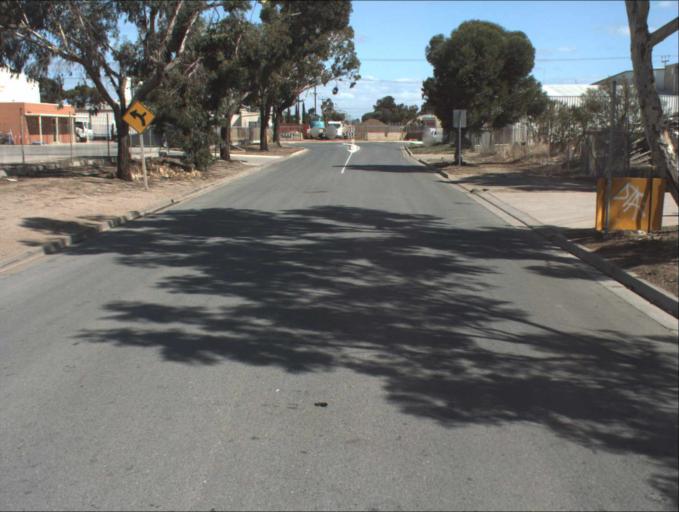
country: AU
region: South Australia
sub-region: Charles Sturt
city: Woodville North
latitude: -34.8385
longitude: 138.5504
